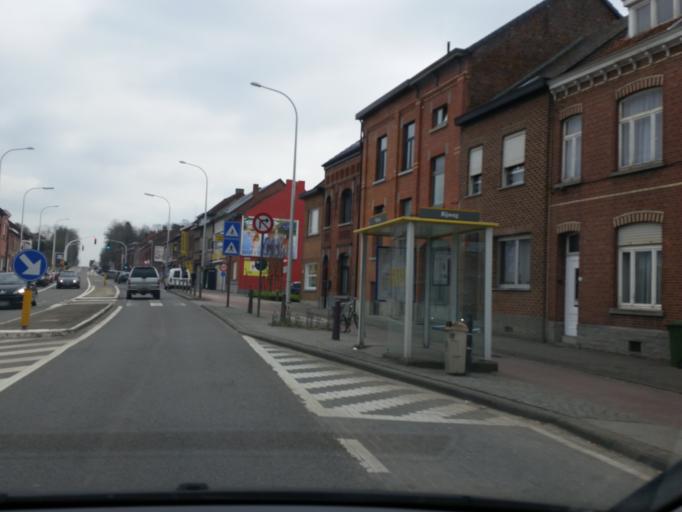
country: BE
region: Flanders
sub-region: Provincie Vlaams-Brabant
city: Herent
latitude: 50.8998
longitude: 4.6801
